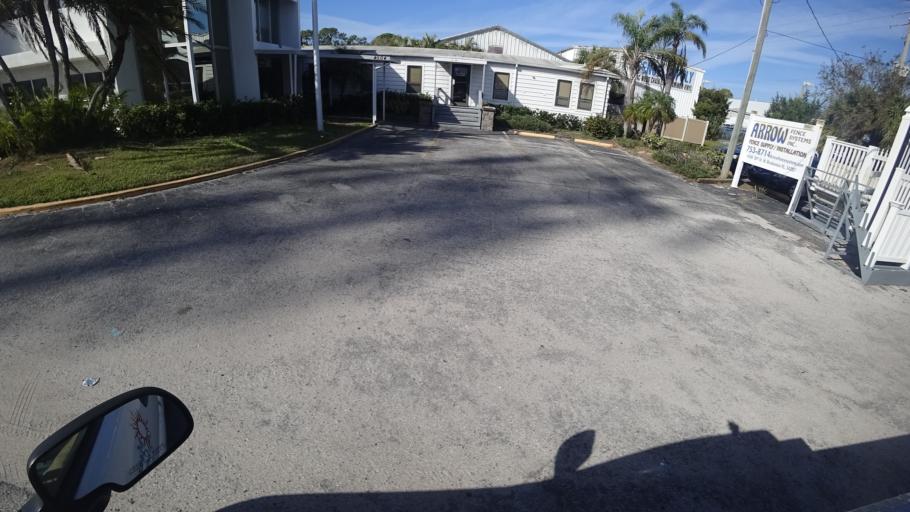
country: US
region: Florida
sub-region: Manatee County
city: South Bradenton
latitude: 27.4613
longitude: -82.5918
